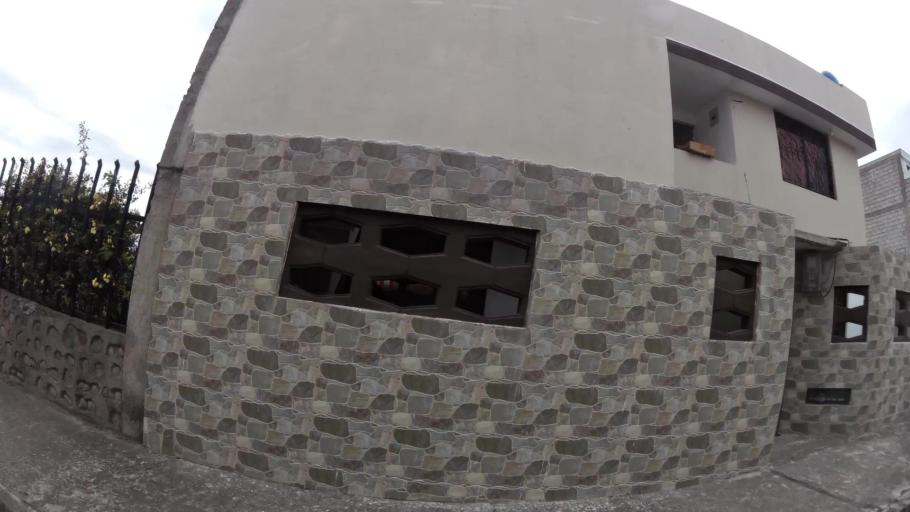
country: EC
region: Cotopaxi
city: Latacunga
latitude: -0.9534
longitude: -78.6041
